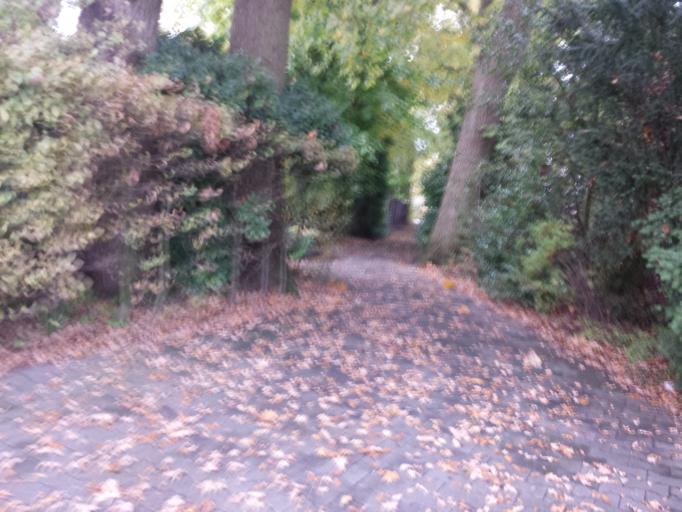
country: DE
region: North Rhine-Westphalia
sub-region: Regierungsbezirk Detmold
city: Guetersloh
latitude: 51.9197
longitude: 8.3633
